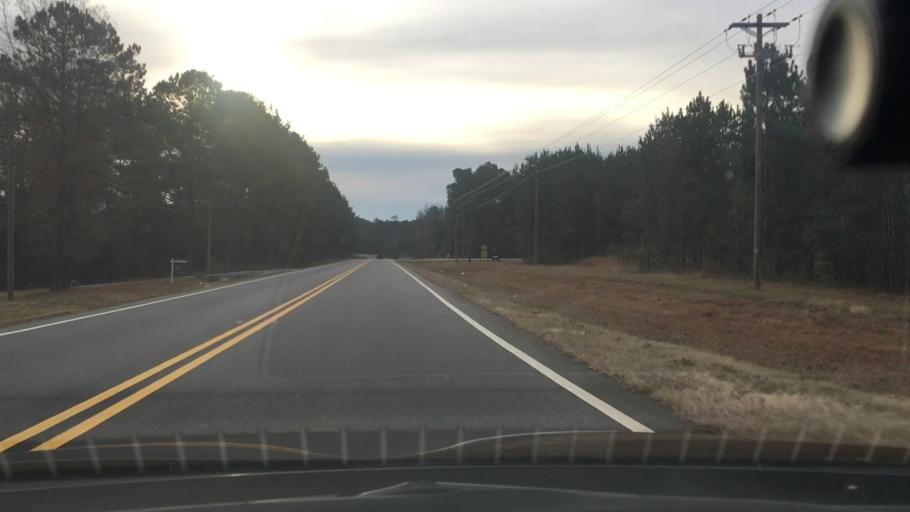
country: US
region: Georgia
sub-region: Coweta County
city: Senoia
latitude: 33.2669
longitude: -84.5225
